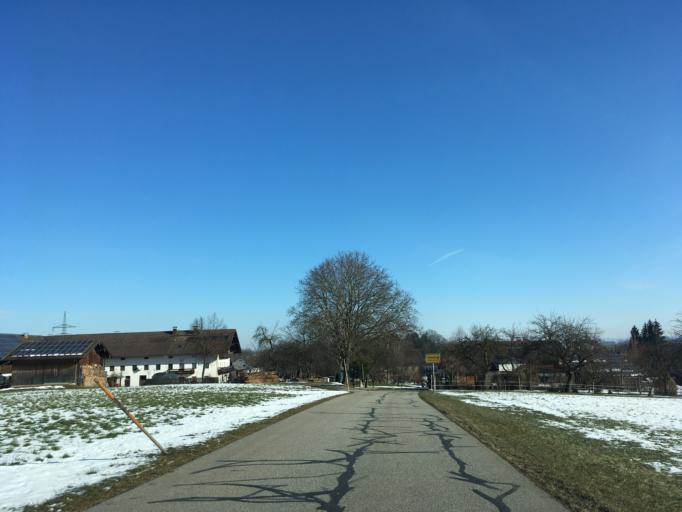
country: DE
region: Bavaria
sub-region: Upper Bavaria
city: Vogtareuth
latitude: 47.9286
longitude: 12.1617
